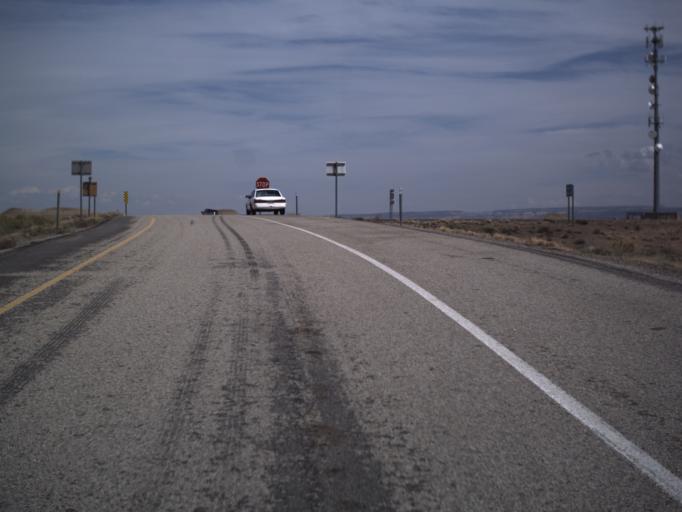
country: US
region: Utah
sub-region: Grand County
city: Moab
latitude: 38.9371
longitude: -109.4085
